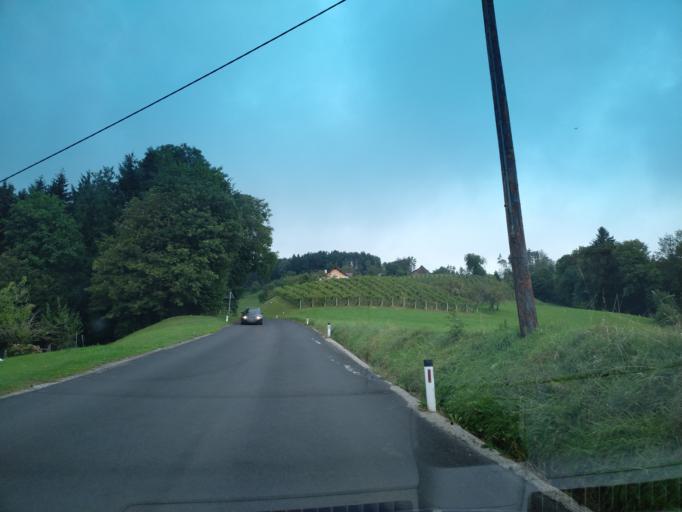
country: AT
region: Styria
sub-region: Politischer Bezirk Deutschlandsberg
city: Deutschlandsberg
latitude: 46.8280
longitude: 15.1985
